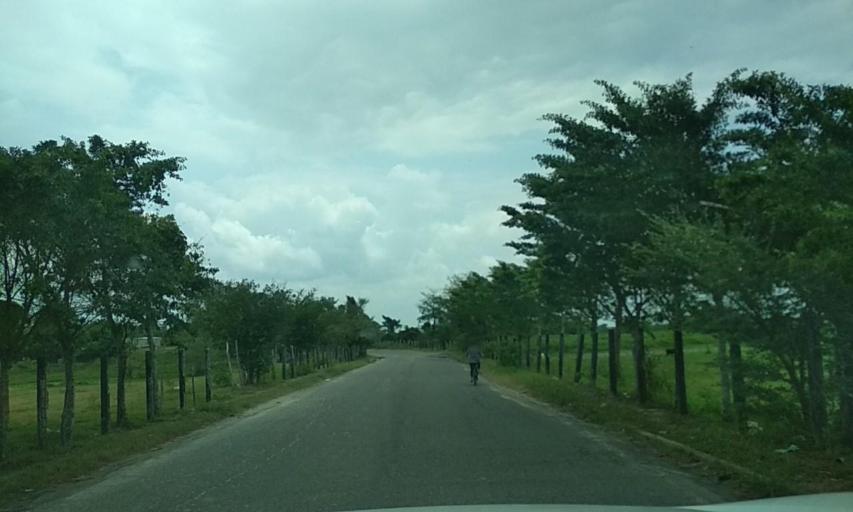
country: MX
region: Veracruz
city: Las Choapas
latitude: 17.8952
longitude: -94.0936
